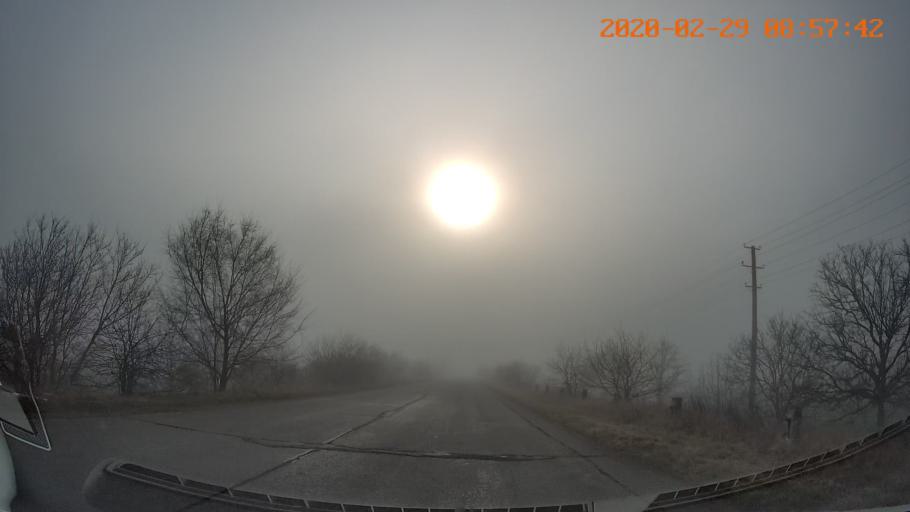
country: MD
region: Telenesti
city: Tiraspolul Nou
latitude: 46.9264
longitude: 29.6302
